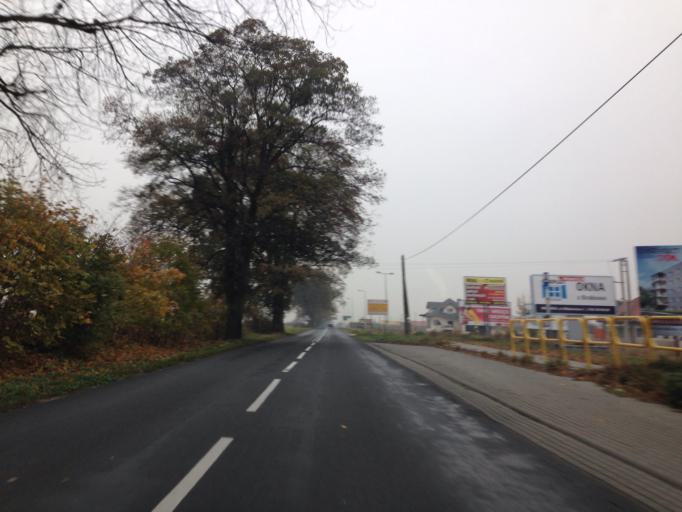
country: PL
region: Kujawsko-Pomorskie
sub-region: Powiat brodnicki
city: Brodnica
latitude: 53.2503
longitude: 19.4476
